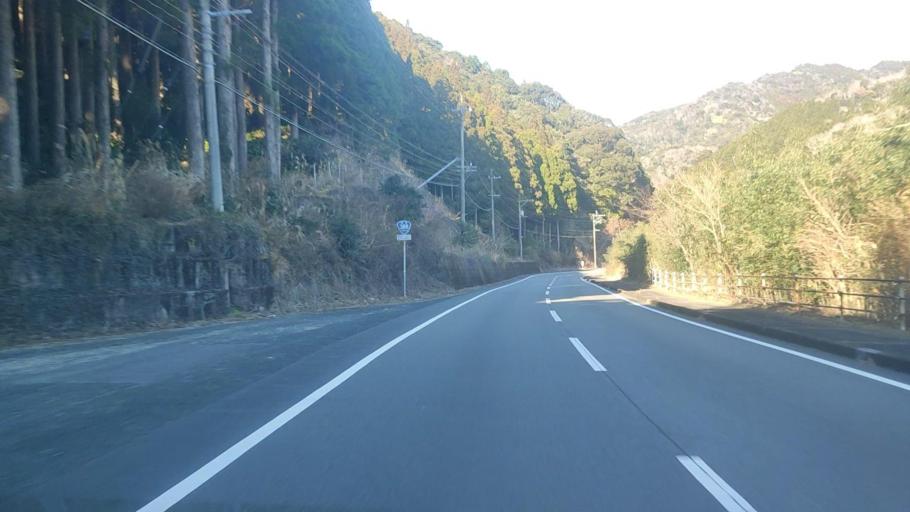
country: JP
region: Oita
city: Saiki
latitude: 32.7423
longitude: 131.8226
